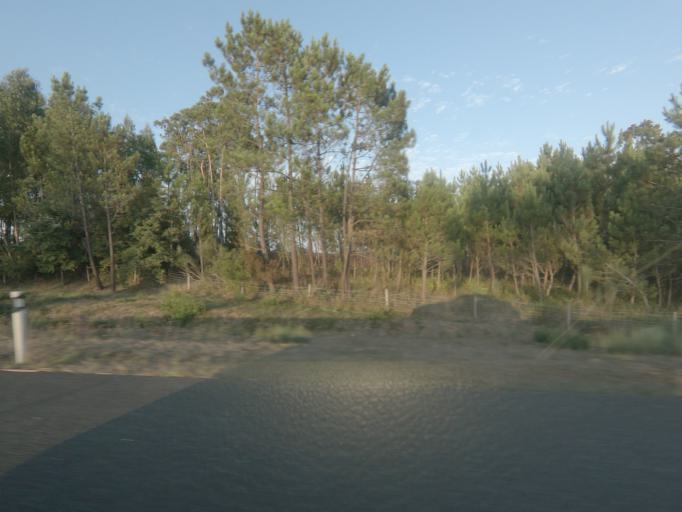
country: PT
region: Leiria
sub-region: Leiria
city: Santa Catarina da Serra
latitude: 39.6522
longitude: -8.6960
